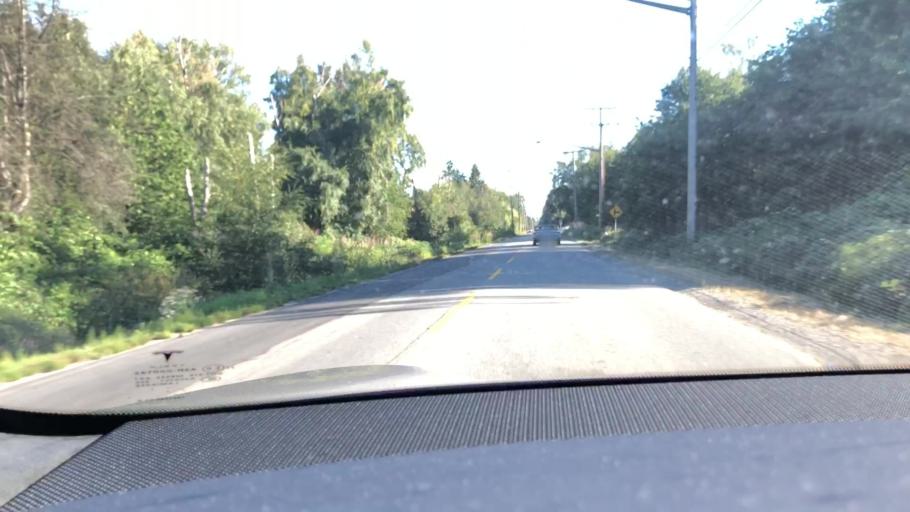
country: CA
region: British Columbia
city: Richmond
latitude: 49.1572
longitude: -123.0689
